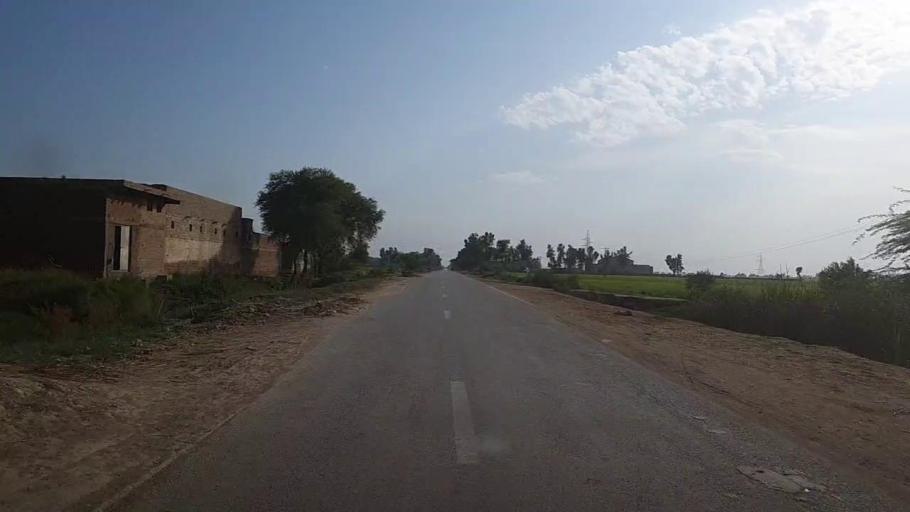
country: PK
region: Sindh
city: Thul
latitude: 28.2299
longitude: 68.7660
